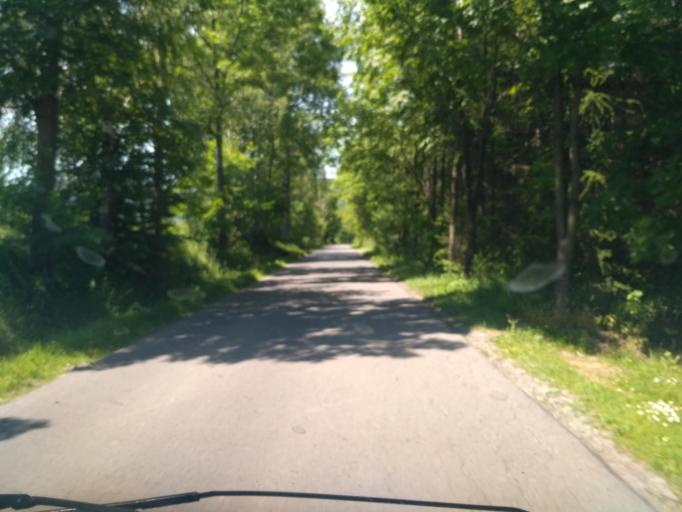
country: PL
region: Subcarpathian Voivodeship
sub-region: Powiat strzyzowski
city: Polomia
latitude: 49.8933
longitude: 21.8496
